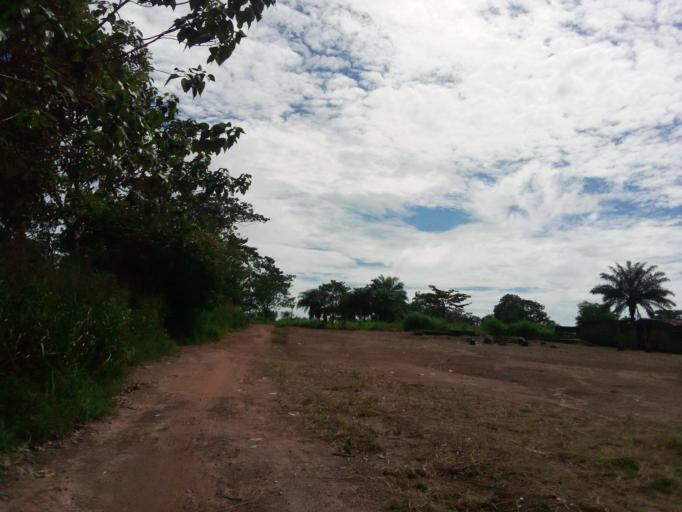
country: SL
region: Eastern Province
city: Koidu
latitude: 8.6536
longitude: -10.9583
